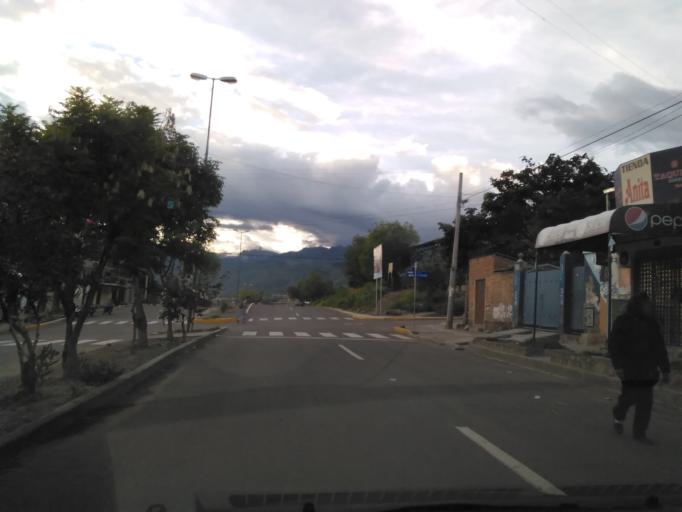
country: BO
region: Cochabamba
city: Cochabamba
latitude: -17.3523
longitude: -66.1606
